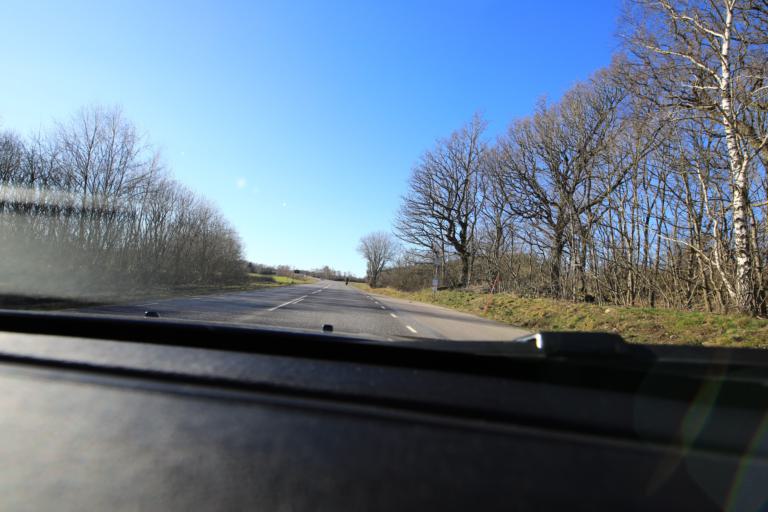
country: SE
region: Halland
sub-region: Varbergs Kommun
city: Tvaaker
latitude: 57.0482
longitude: 12.3755
